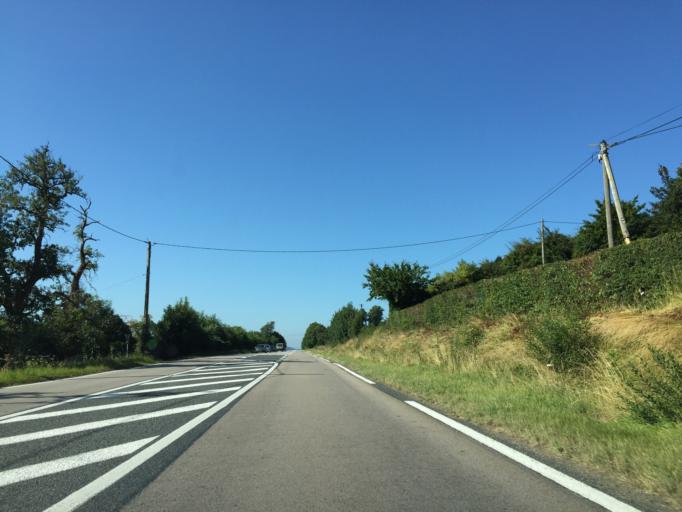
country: FR
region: Lower Normandy
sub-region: Departement du Calvados
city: Lisieux
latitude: 49.1694
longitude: 0.2276
